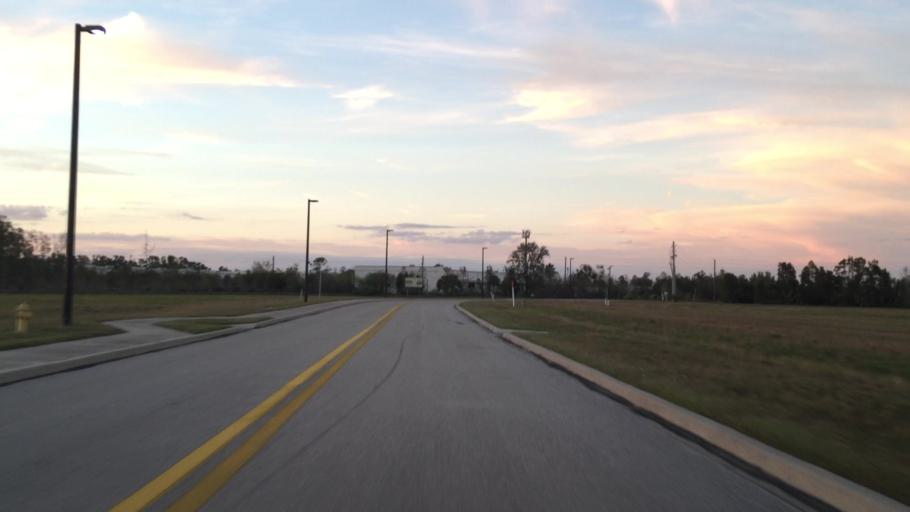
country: US
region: Florida
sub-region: Lee County
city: Three Oaks
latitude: 26.5309
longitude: -81.7911
